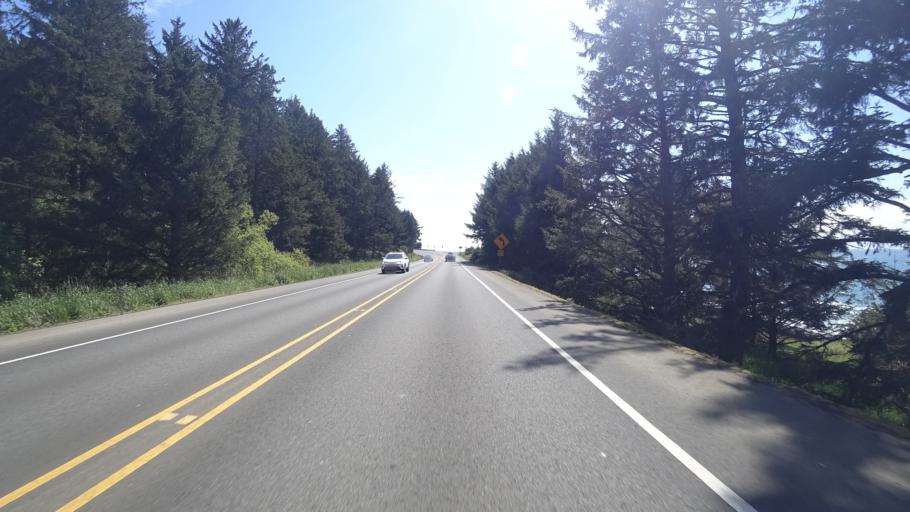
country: US
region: Oregon
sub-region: Lincoln County
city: Depoe Bay
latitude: 44.7836
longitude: -124.0724
